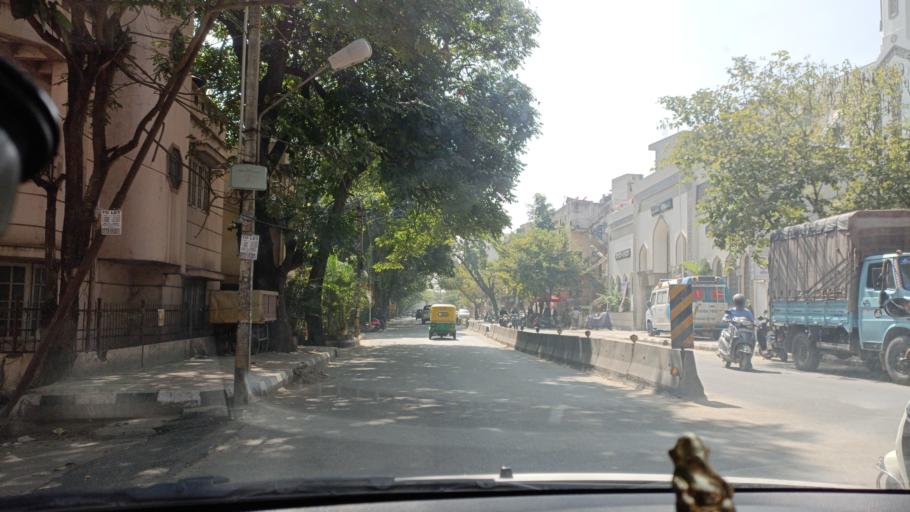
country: IN
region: Karnataka
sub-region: Bangalore Urban
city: Bangalore
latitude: 12.9085
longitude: 77.6138
